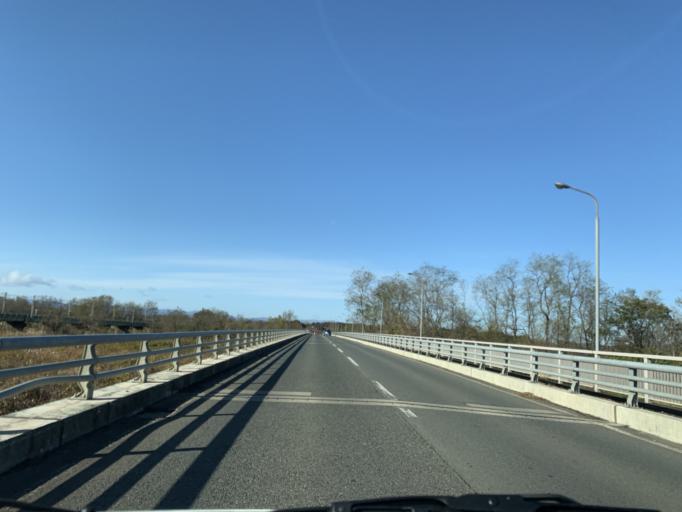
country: JP
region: Iwate
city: Mizusawa
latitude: 39.1851
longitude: 141.1279
